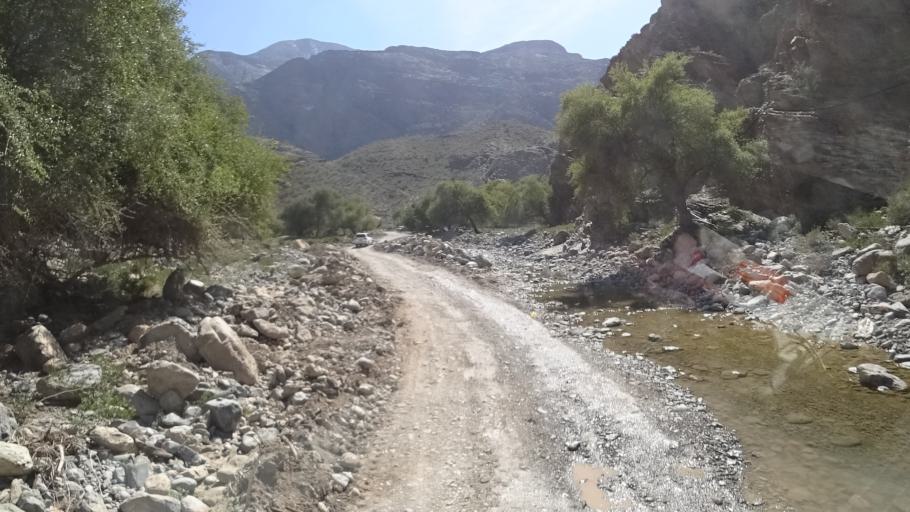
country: OM
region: Al Batinah
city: Bayt al `Awabi
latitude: 23.2191
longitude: 57.4074
